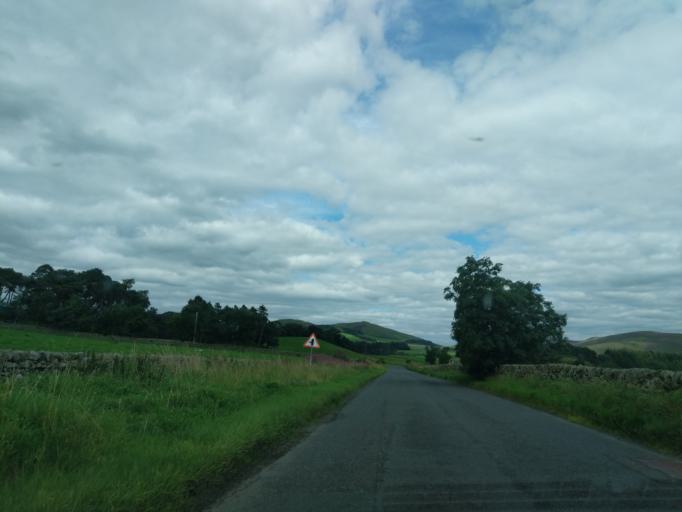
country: GB
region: Scotland
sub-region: The Scottish Borders
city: Peebles
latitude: 55.6413
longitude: -3.2813
